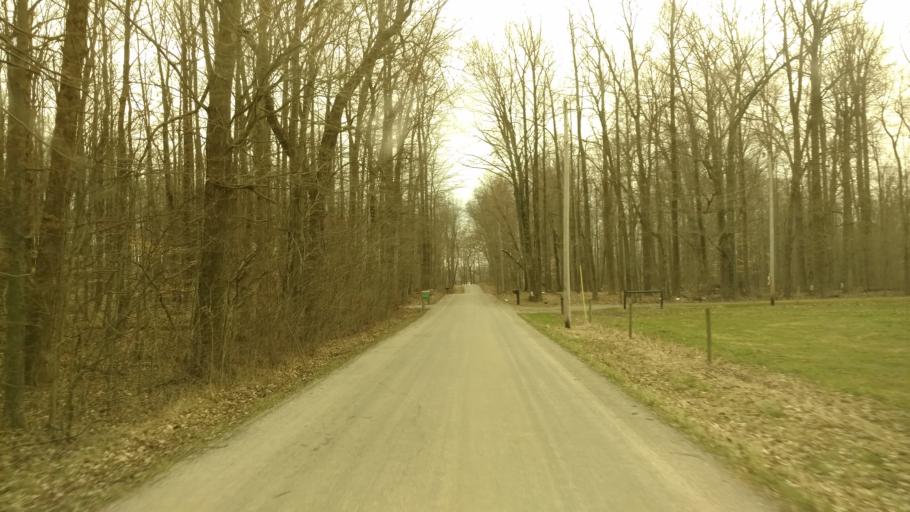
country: US
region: Ohio
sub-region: Morrow County
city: Mount Gilead
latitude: 40.5543
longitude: -82.7773
